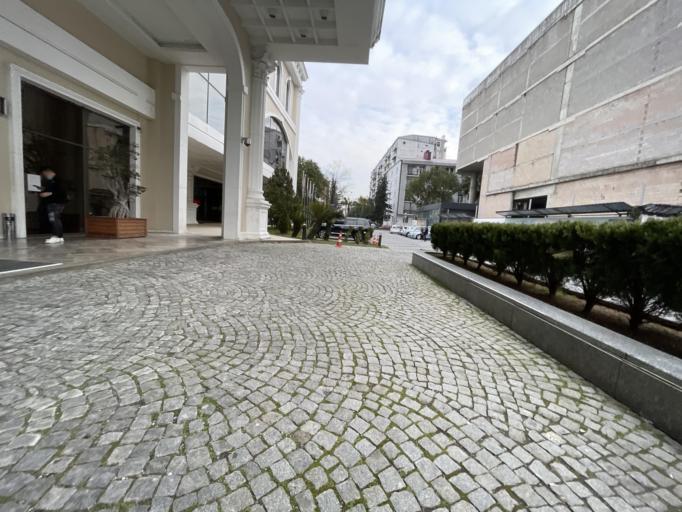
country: GE
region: Ajaria
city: Batumi
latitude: 41.6507
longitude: 41.6297
